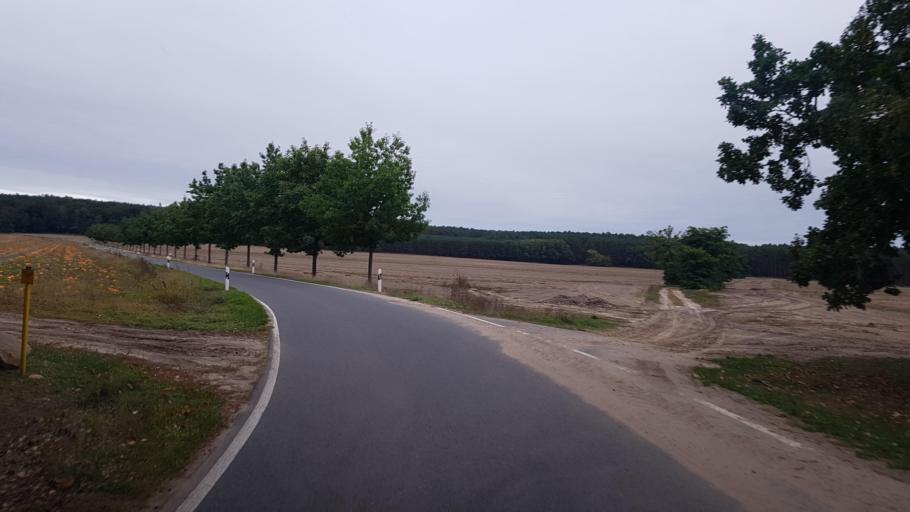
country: DE
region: Brandenburg
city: Drahnsdorf
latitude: 51.9493
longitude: 13.5448
